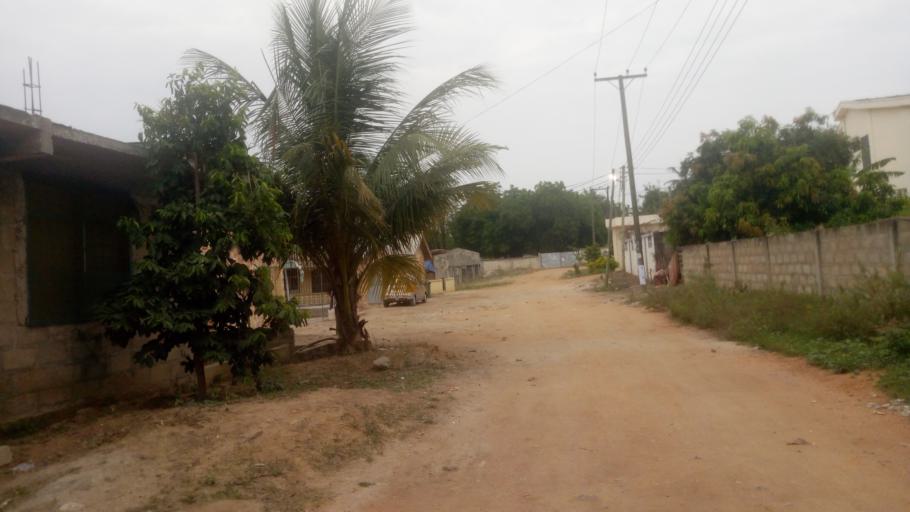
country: GH
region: Central
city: Winneba
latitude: 5.3606
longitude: -0.6294
